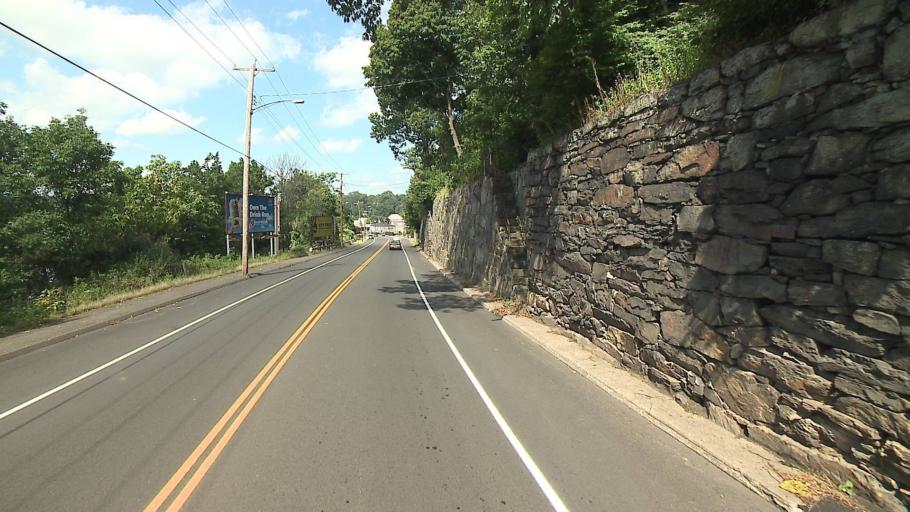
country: US
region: Connecticut
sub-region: New Haven County
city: Ansonia
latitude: 41.3333
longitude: -73.0765
